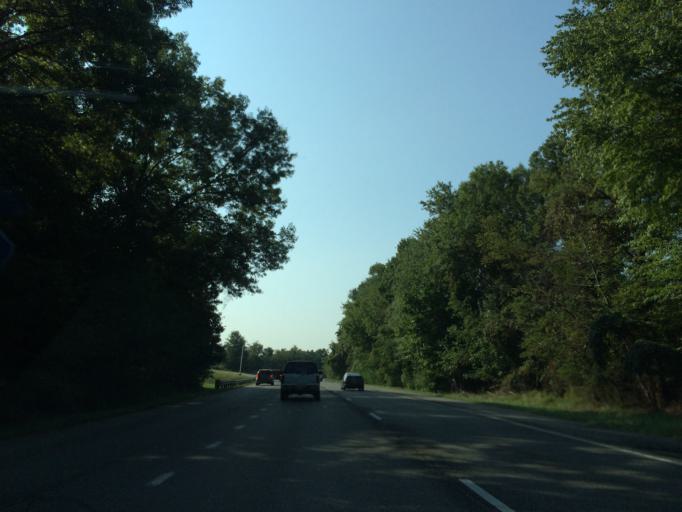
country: US
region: Maryland
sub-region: Prince George's County
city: Mitchellville
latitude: 38.8903
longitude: -76.7215
